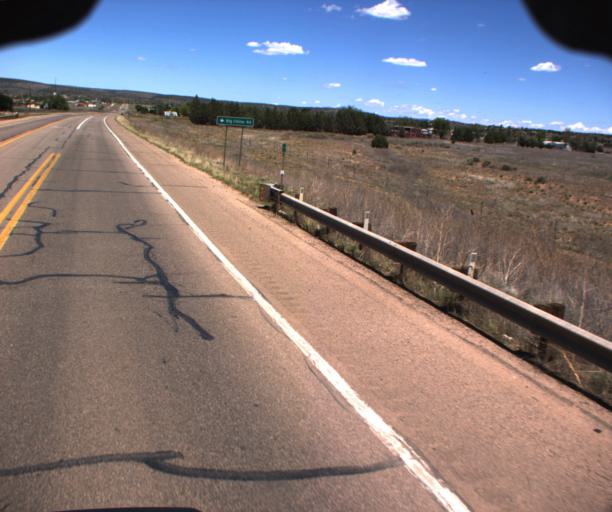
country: US
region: Arizona
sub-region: Yavapai County
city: Paulden
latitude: 34.8935
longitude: -112.4668
